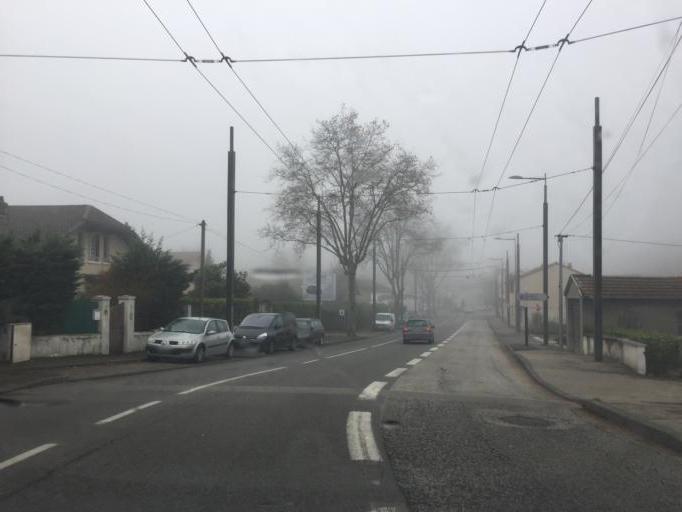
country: FR
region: Rhone-Alpes
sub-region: Departement du Rhone
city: Caluire-et-Cuire
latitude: 45.7993
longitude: 4.8528
